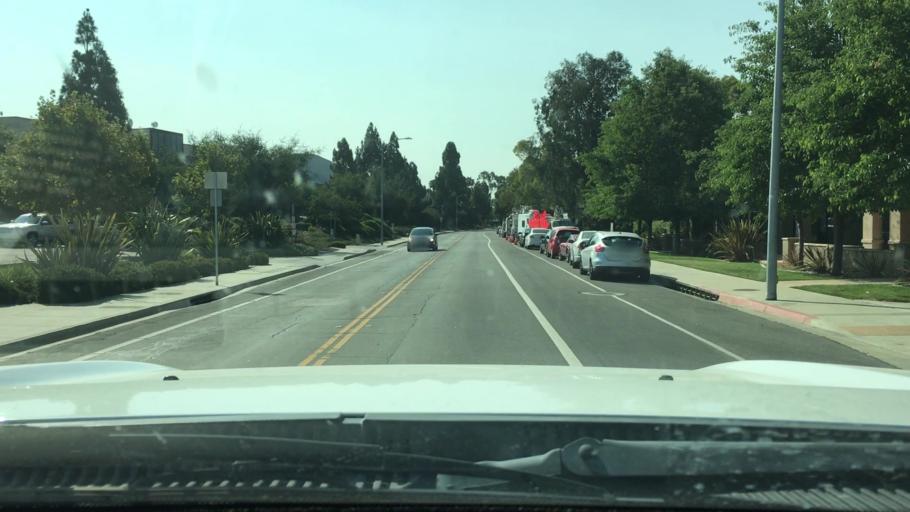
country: US
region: California
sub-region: San Luis Obispo County
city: San Luis Obispo
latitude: 35.2557
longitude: -120.6426
